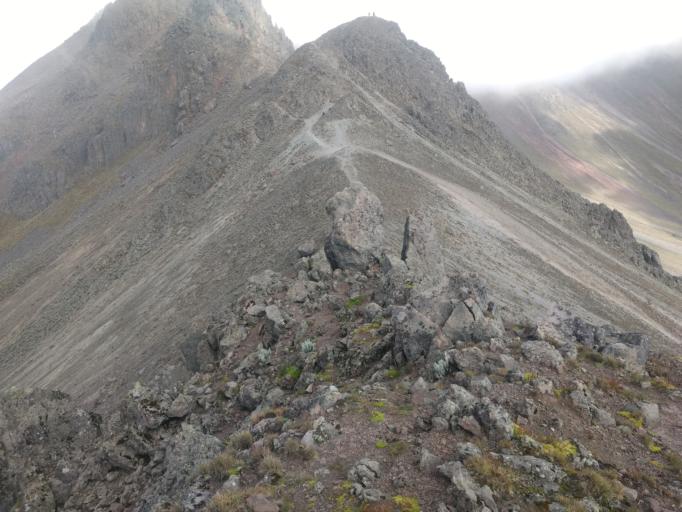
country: MX
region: Mexico
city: Cerro La Calera
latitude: 19.1005
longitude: -99.7595
